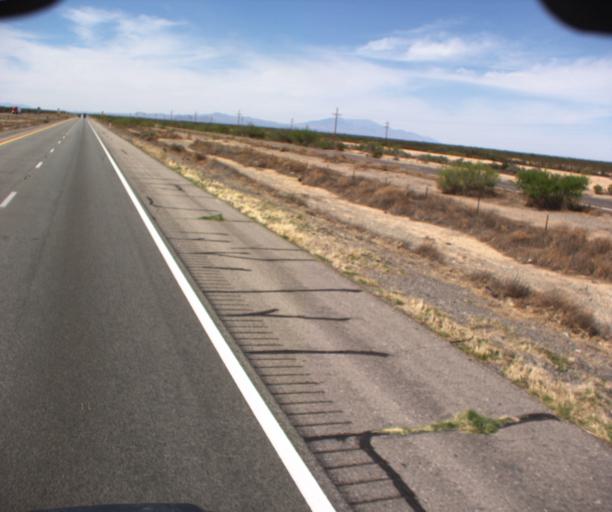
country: US
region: Arizona
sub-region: Cochise County
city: Willcox
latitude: 32.2876
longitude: -109.3108
